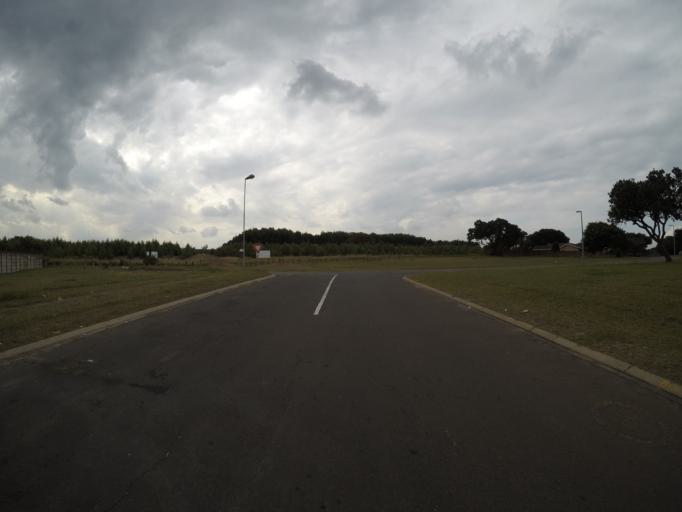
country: ZA
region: KwaZulu-Natal
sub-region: uThungulu District Municipality
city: Richards Bay
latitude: -28.7310
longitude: 32.0513
